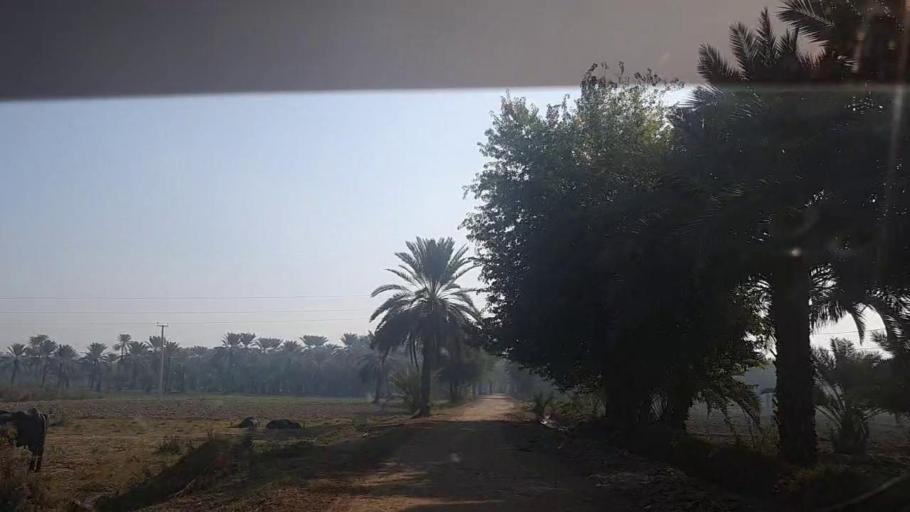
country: PK
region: Sindh
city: Khairpur
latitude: 27.4766
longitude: 68.7229
